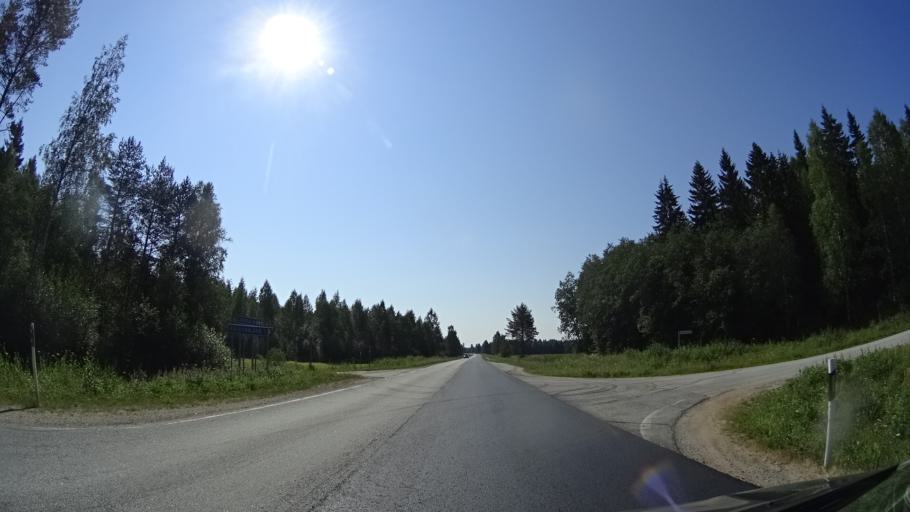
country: FI
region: North Karelia
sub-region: Joensuu
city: Juuka
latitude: 63.2176
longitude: 29.3018
